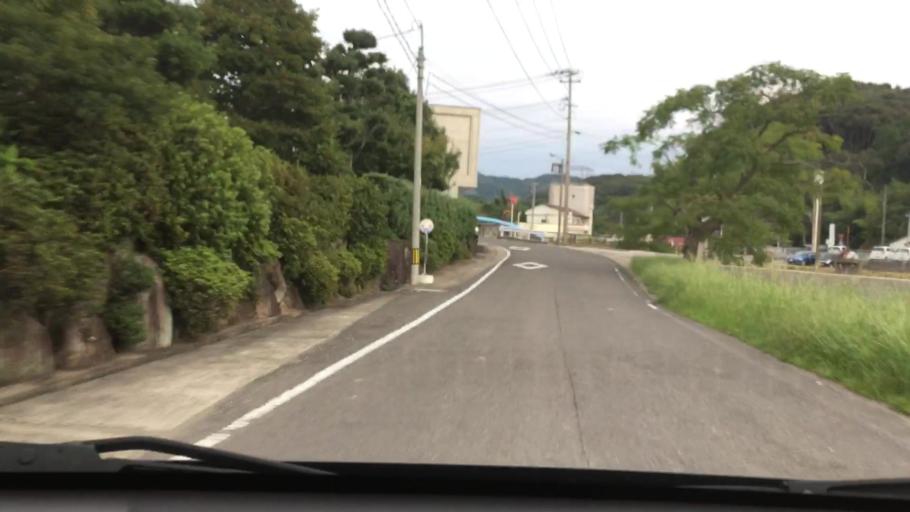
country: JP
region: Nagasaki
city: Togitsu
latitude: 32.9883
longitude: 129.7736
